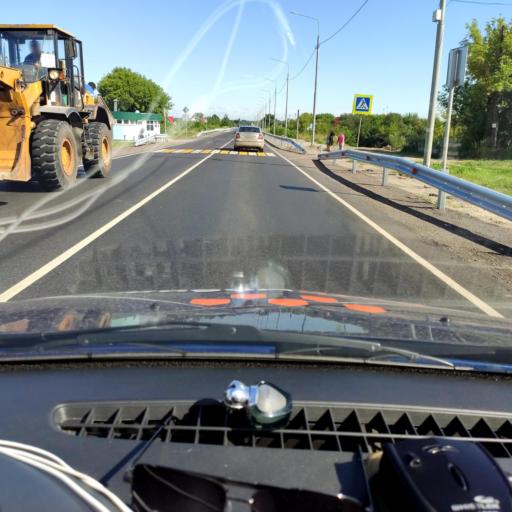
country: RU
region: Lipetsk
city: Khlevnoye
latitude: 52.1205
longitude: 39.1662
